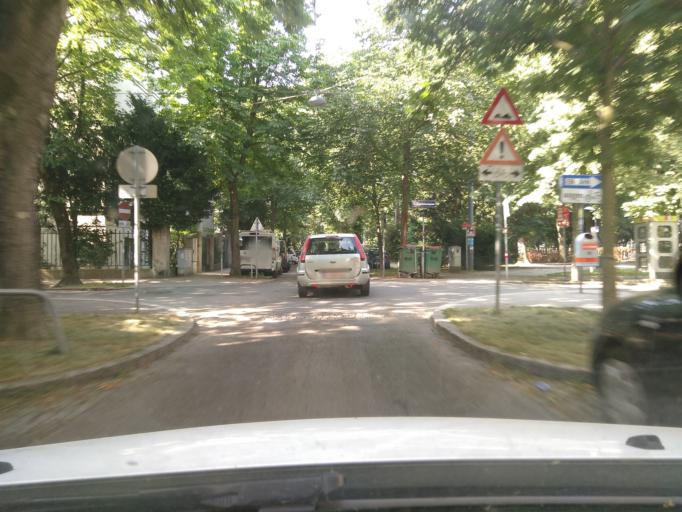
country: AT
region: Lower Austria
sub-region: Politischer Bezirk Modling
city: Perchtoldsdorf
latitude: 48.1860
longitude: 16.2885
